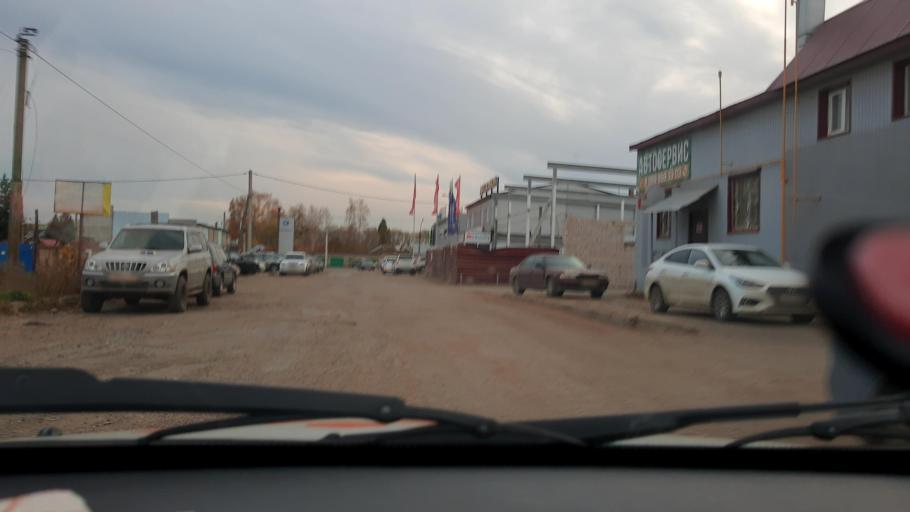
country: RU
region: Bashkortostan
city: Ufa
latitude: 54.8250
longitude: 56.0999
